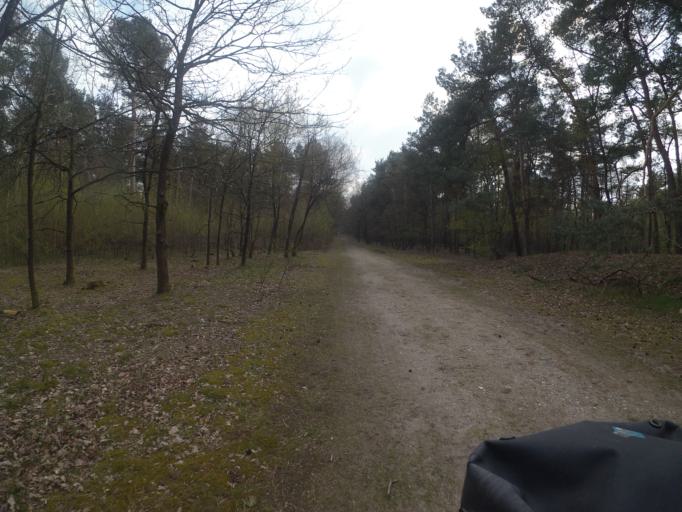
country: NL
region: North Brabant
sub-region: Gemeente Oss
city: Berghem
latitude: 51.7608
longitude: 5.5913
